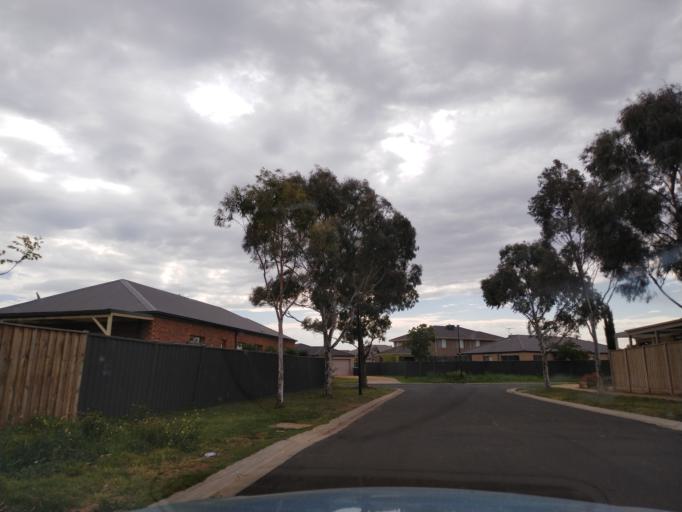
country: AU
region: Victoria
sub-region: Wyndham
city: Williams Landing
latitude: -37.8380
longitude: 144.7109
